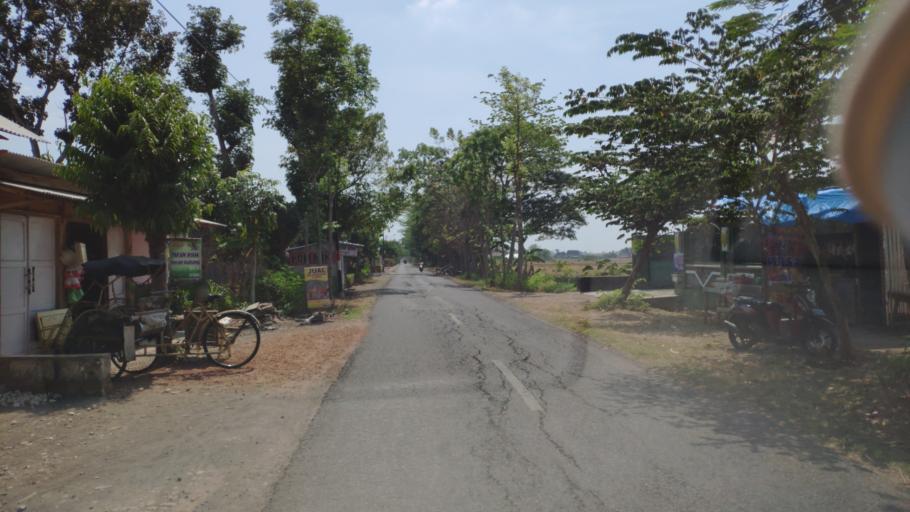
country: ID
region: Central Java
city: Kedungjenar
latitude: -6.9807
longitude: 111.4294
